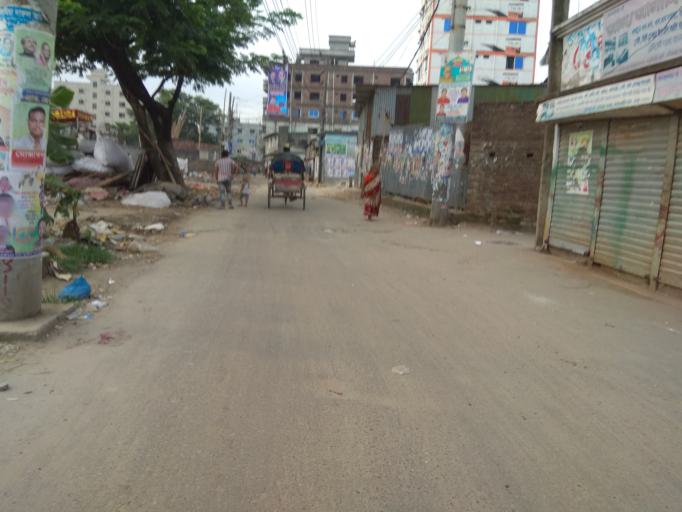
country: BD
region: Dhaka
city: Azimpur
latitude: 23.7137
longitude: 90.3783
